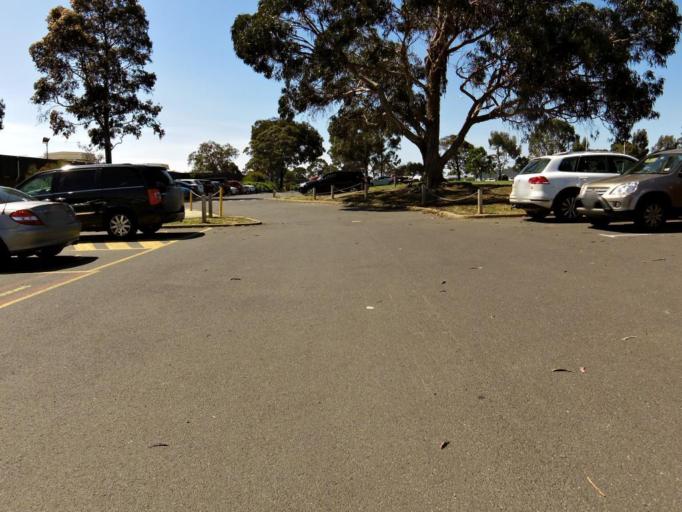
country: AU
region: Victoria
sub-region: Whitehorse
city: Blackburn South
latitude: -37.8494
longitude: 145.1622
